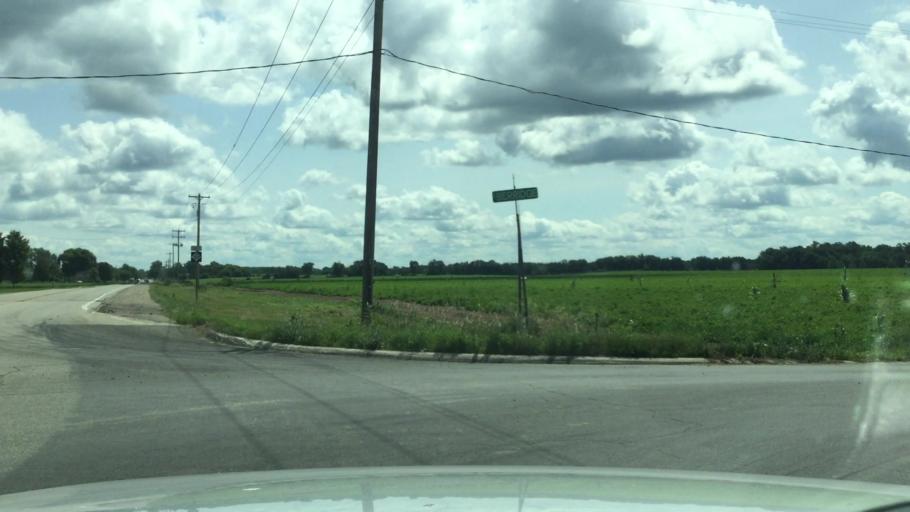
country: US
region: Michigan
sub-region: Montcalm County
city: Greenville
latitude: 43.1705
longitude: -85.2135
